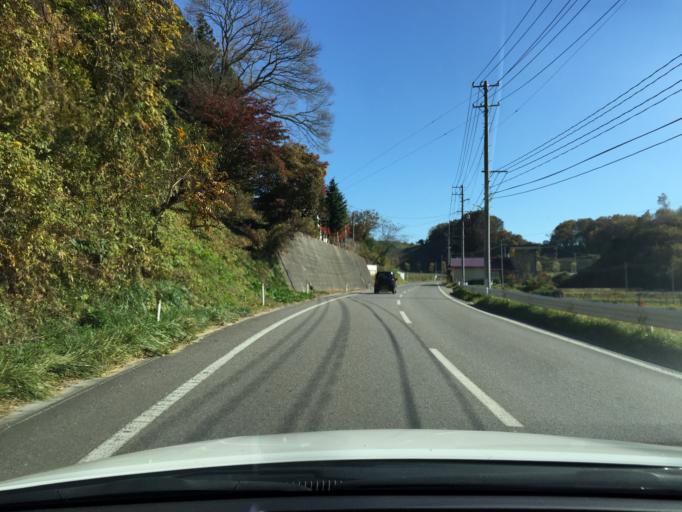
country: JP
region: Fukushima
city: Miharu
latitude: 37.4358
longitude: 140.5112
